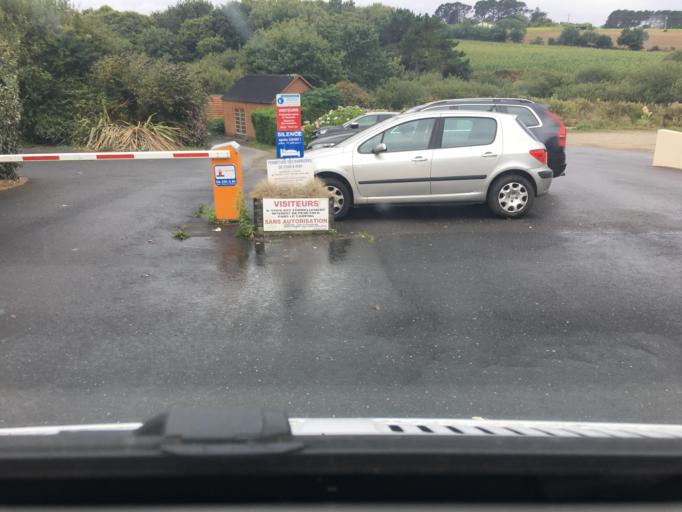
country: FR
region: Brittany
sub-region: Departement du Finistere
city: Beuzec-Cap-Sizun
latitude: 48.0842
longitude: -4.4821
